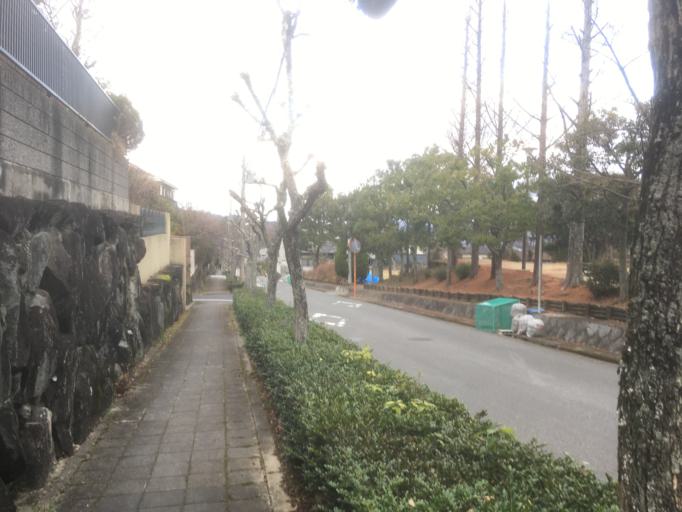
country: JP
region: Nara
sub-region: Ikoma-shi
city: Ikoma
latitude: 34.6990
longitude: 135.6879
